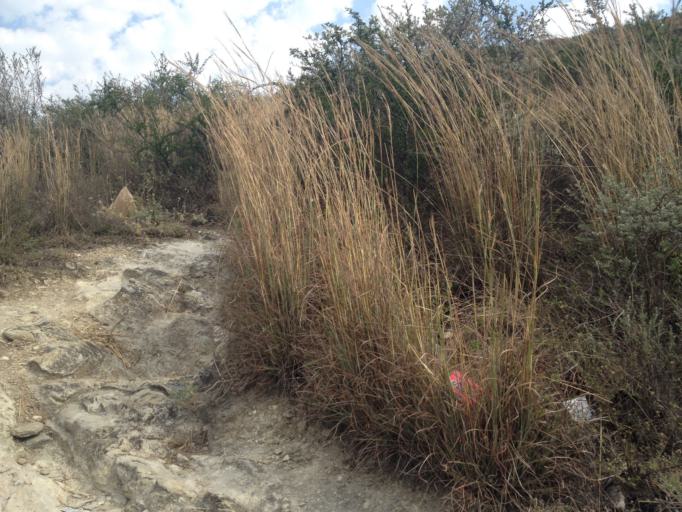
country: MX
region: Nuevo Leon
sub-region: Monterrey
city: Monterrey
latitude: 25.6537
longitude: -100.3316
